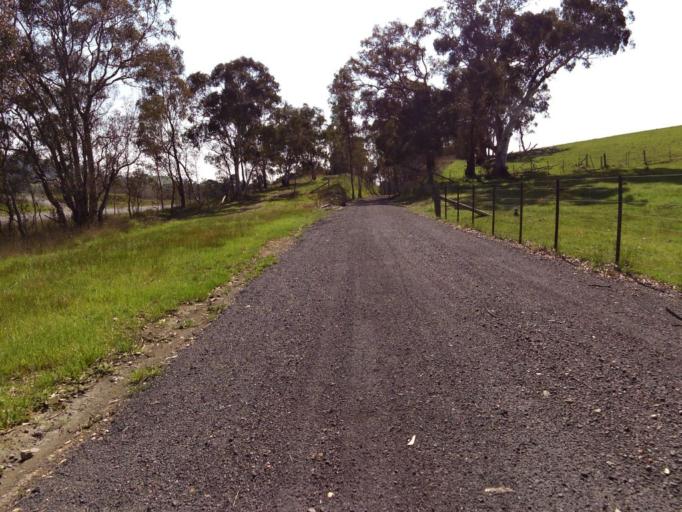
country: AU
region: Victoria
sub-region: Murrindindi
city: Alexandra
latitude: -37.1325
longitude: 145.5933
